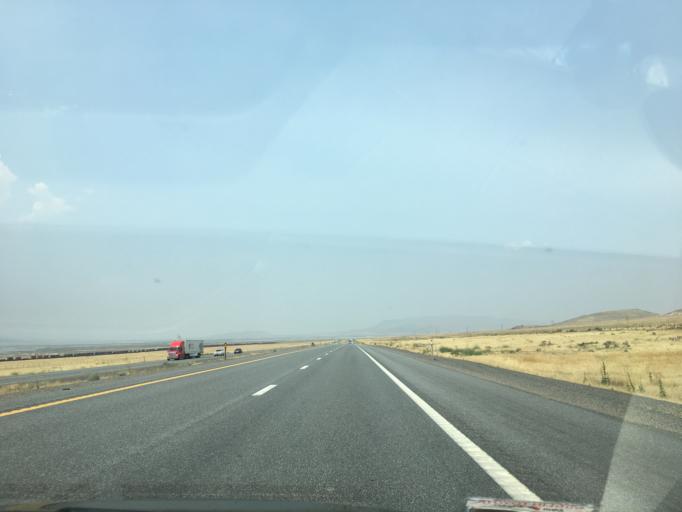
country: US
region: Nevada
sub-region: Pershing County
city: Lovelock
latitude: 40.5372
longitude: -118.2782
